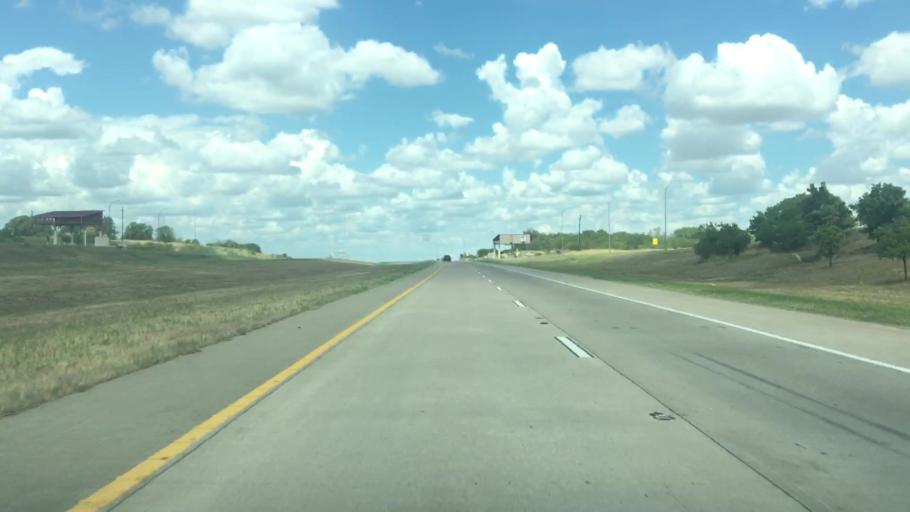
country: US
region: Texas
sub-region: Williamson County
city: Georgetown
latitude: 30.6424
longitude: -97.6300
